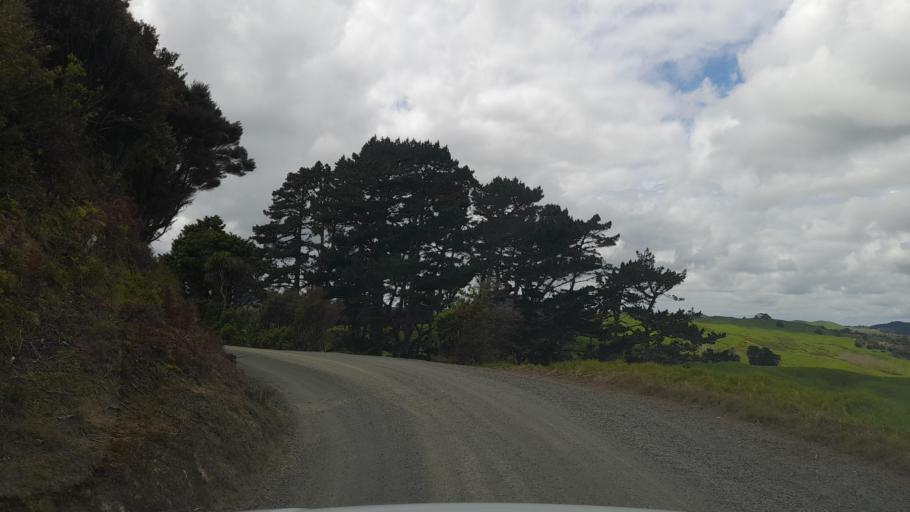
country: NZ
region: Auckland
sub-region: Auckland
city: Wellsford
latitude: -36.1851
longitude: 174.3406
